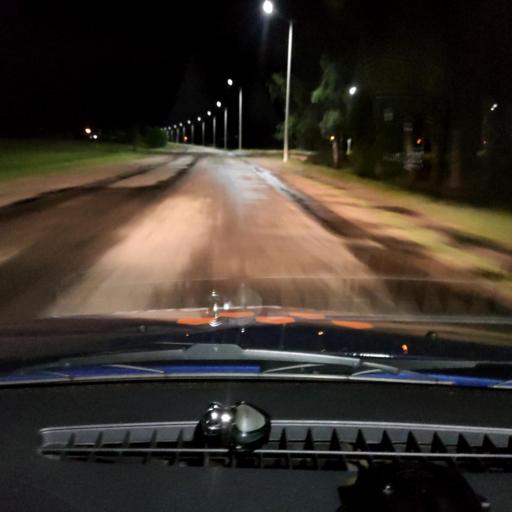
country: RU
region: Voronezj
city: Khrenovoye
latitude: 51.1166
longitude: 40.2638
